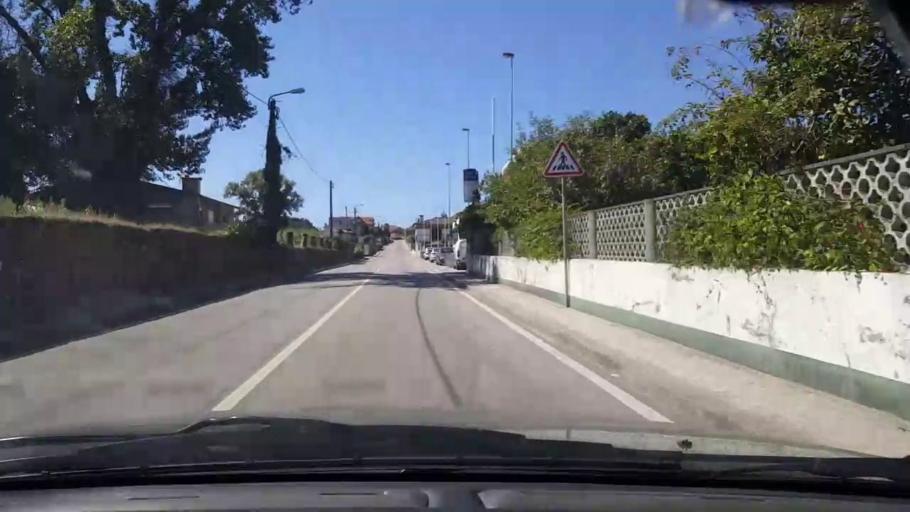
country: PT
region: Porto
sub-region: Vila do Conde
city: Arvore
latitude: 41.3407
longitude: -8.6723
